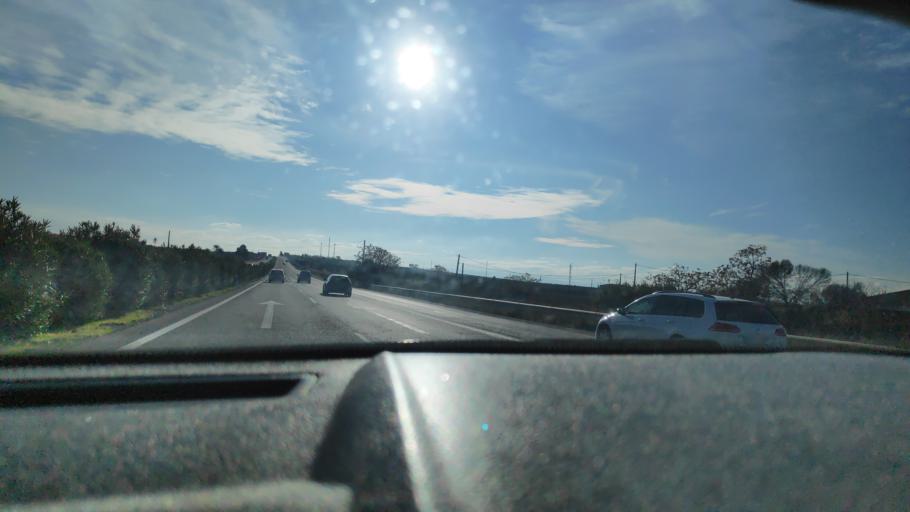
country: ES
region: Andalusia
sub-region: Province of Cordoba
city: La Carlota
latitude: 37.5999
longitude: -4.9739
